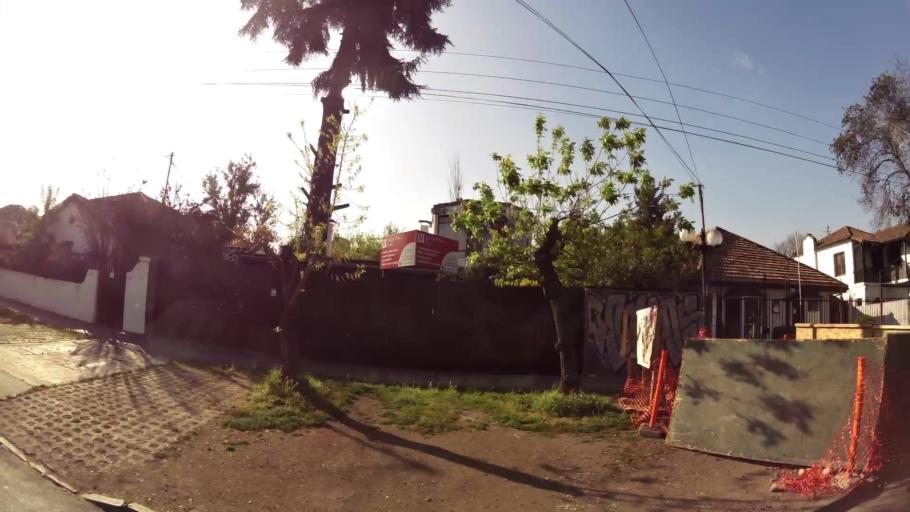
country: CL
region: Santiago Metropolitan
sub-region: Provincia de Santiago
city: Villa Presidente Frei, Nunoa, Santiago, Chile
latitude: -33.4458
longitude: -70.6091
